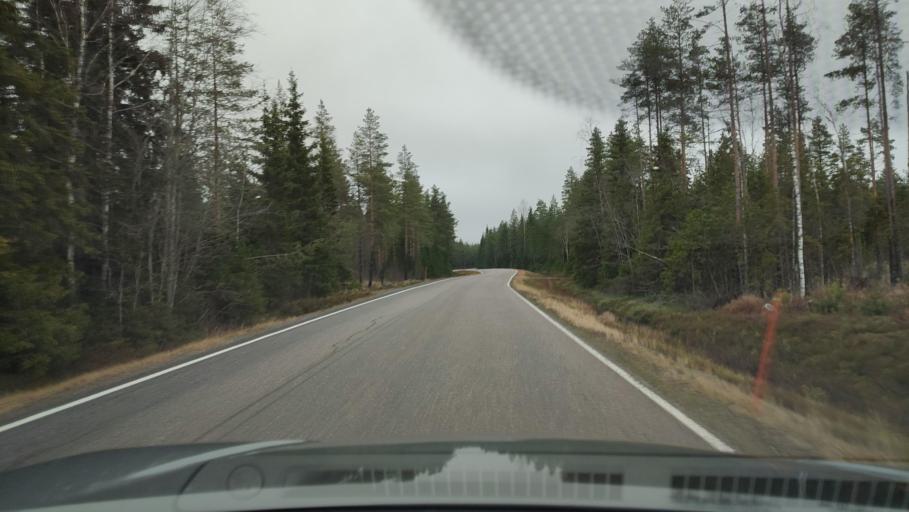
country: FI
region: Southern Ostrobothnia
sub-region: Suupohja
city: Isojoki
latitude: 62.2175
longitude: 21.9907
